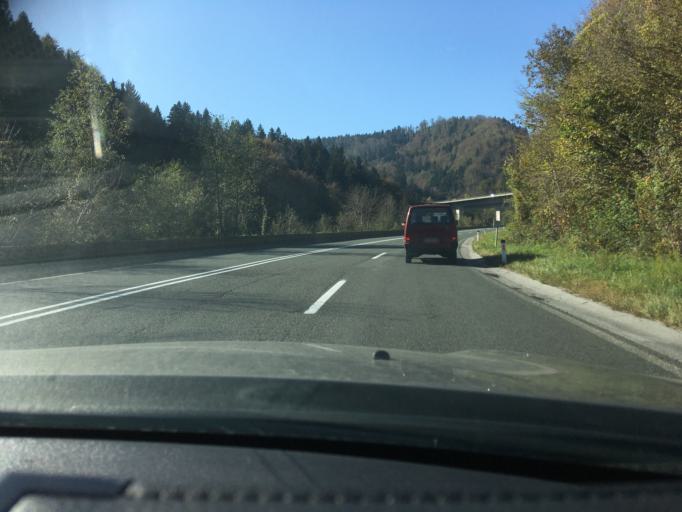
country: SI
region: Vransko
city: Vransko
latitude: 46.2069
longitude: 14.9068
